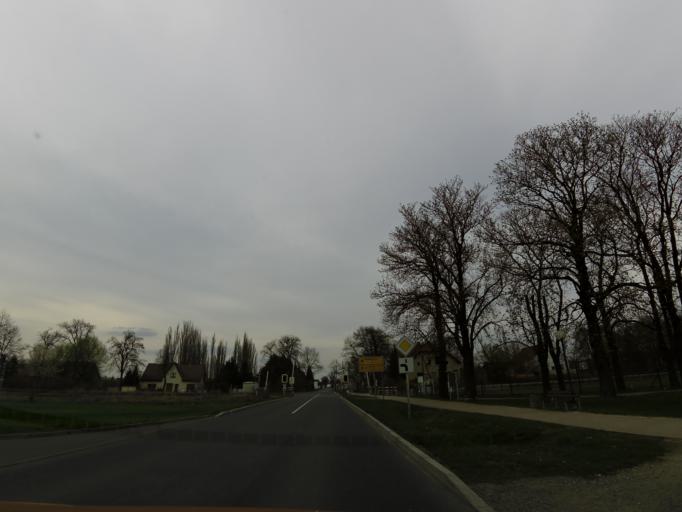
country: DE
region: Brandenburg
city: Rietz Neuendorf
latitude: 52.2034
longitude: 14.1136
